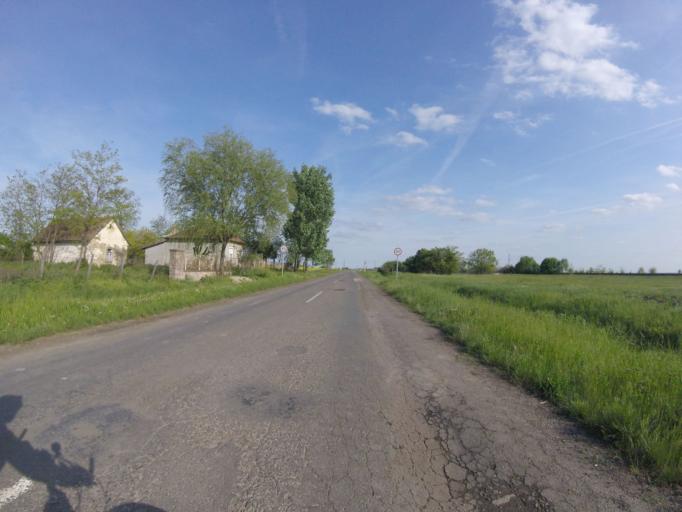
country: HU
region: Pest
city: Tapiogyorgye
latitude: 47.3118
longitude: 19.9727
